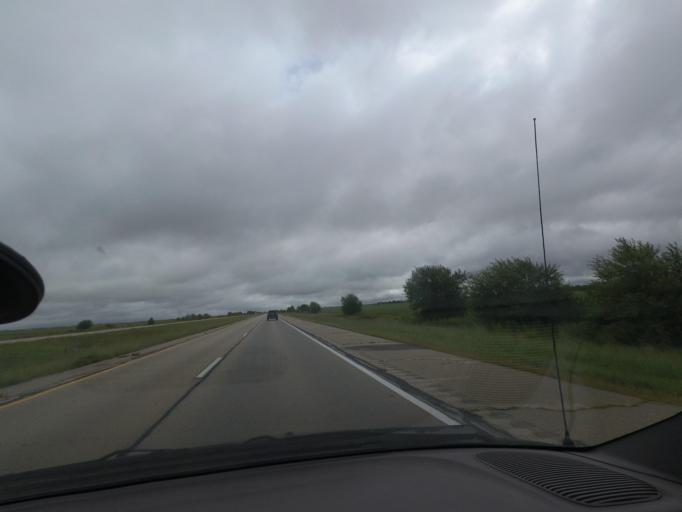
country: US
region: Illinois
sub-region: Piatt County
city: Monticello
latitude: 40.0239
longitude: -88.6853
